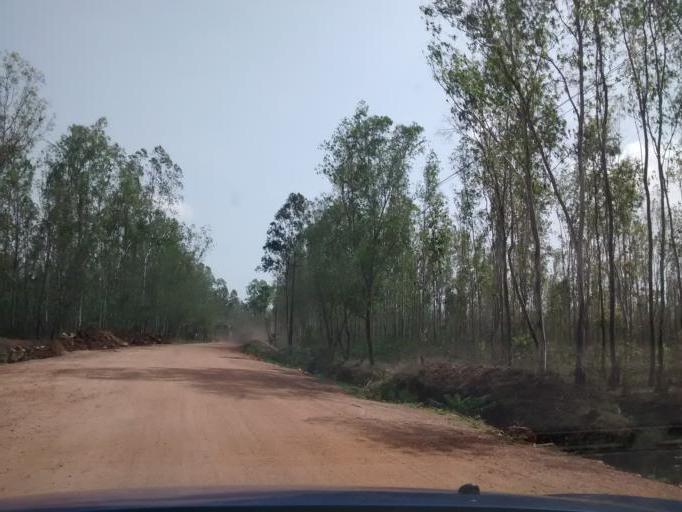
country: IN
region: Karnataka
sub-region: Hassan
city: Arkalgud
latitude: 12.7039
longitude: 76.1503
